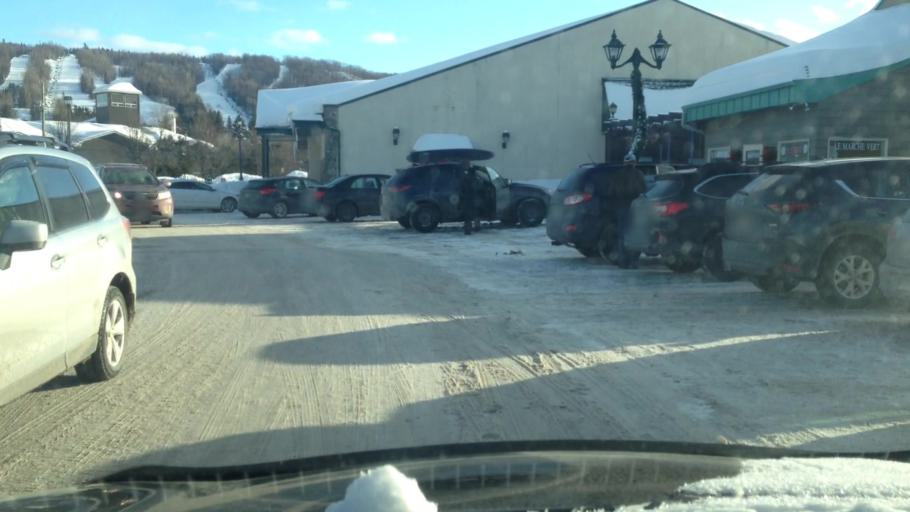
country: CA
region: Quebec
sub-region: Laurentides
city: Saint-Sauveur
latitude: 45.8912
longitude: -74.1544
